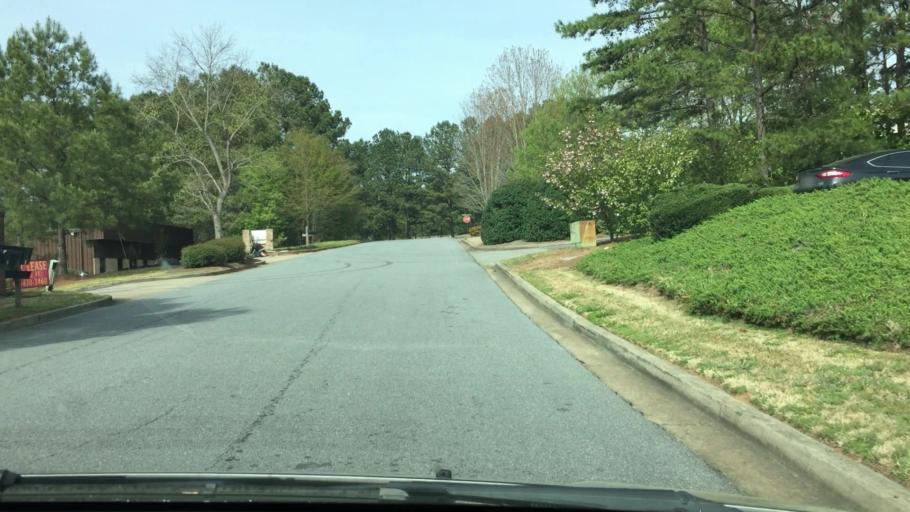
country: US
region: Georgia
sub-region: Fulton County
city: Milton
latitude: 34.1359
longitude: -84.2575
